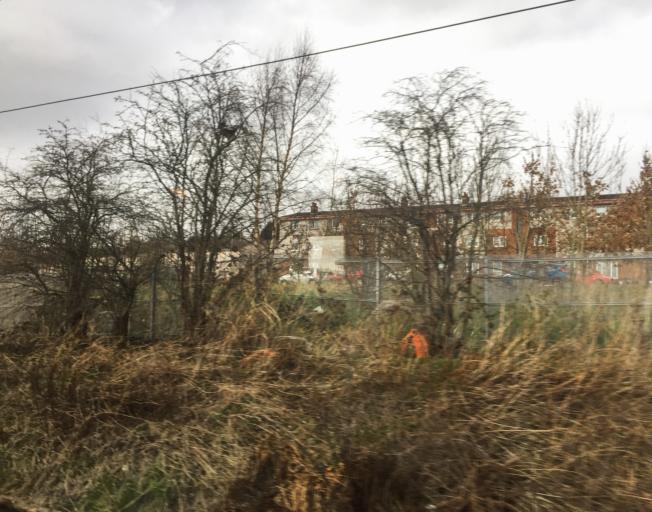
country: GB
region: Scotland
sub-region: West Dunbartonshire
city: Clydebank
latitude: 55.9042
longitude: -4.3890
